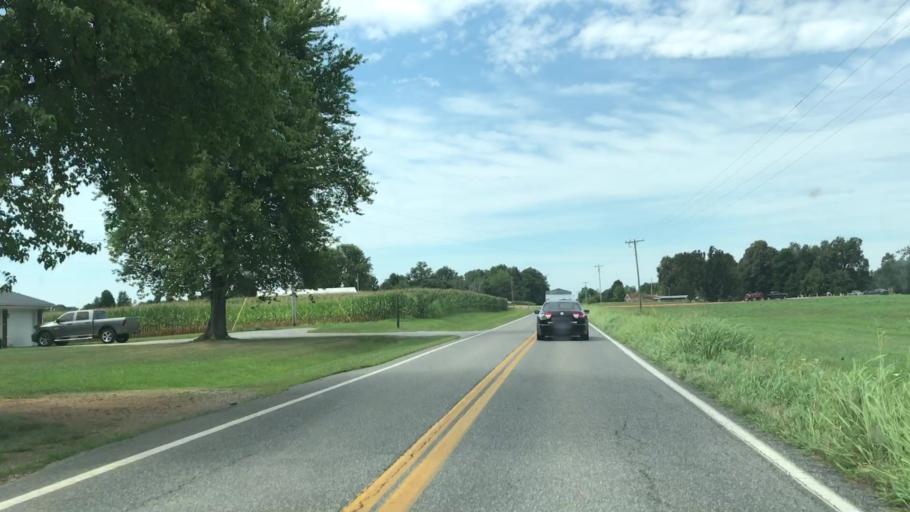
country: US
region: Kentucky
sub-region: Graves County
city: Mayfield
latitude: 36.8509
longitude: -88.5734
